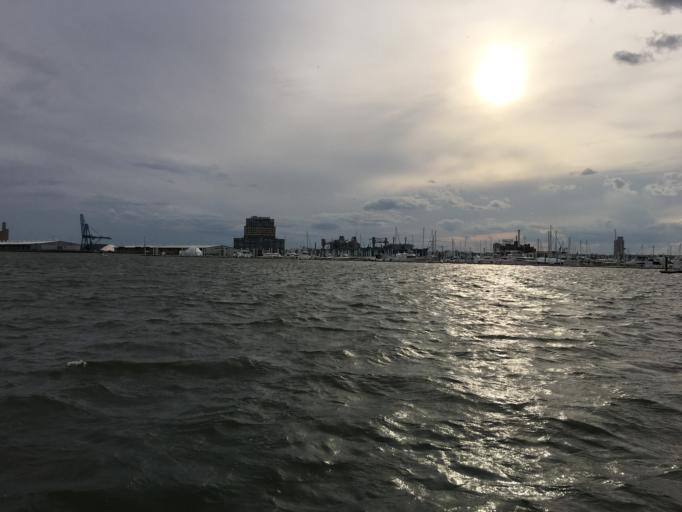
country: US
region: Maryland
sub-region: City of Baltimore
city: Baltimore
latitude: 39.2763
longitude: -76.5745
